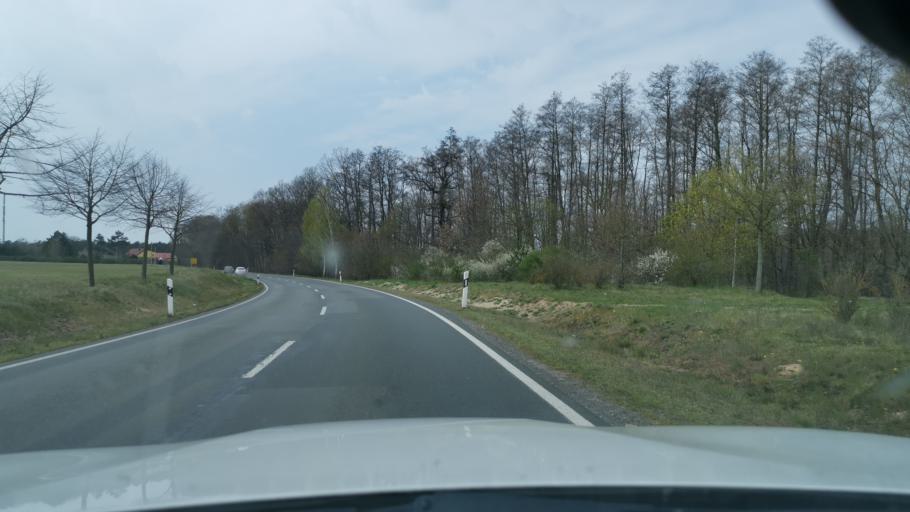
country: DE
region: Saxony
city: Bad Duben
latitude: 51.5672
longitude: 12.5503
